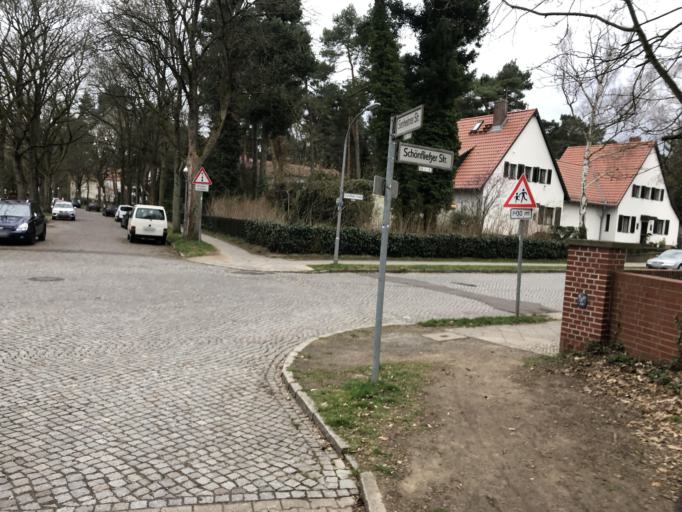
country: DE
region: Berlin
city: Frohnau
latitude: 52.6422
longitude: 13.2921
